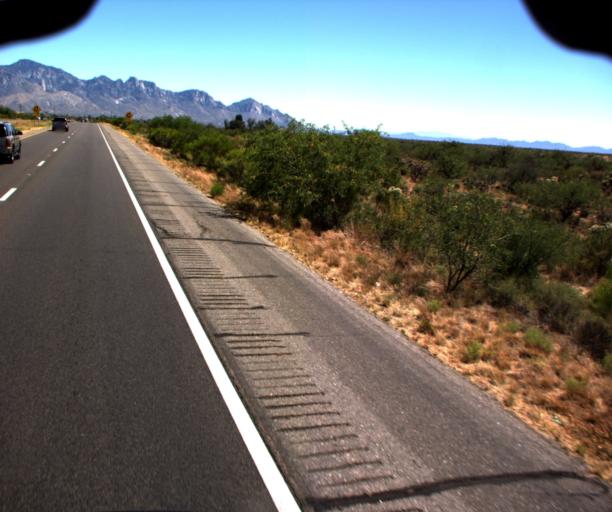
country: US
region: Arizona
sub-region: Pima County
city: Catalina
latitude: 32.5217
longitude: -110.9278
